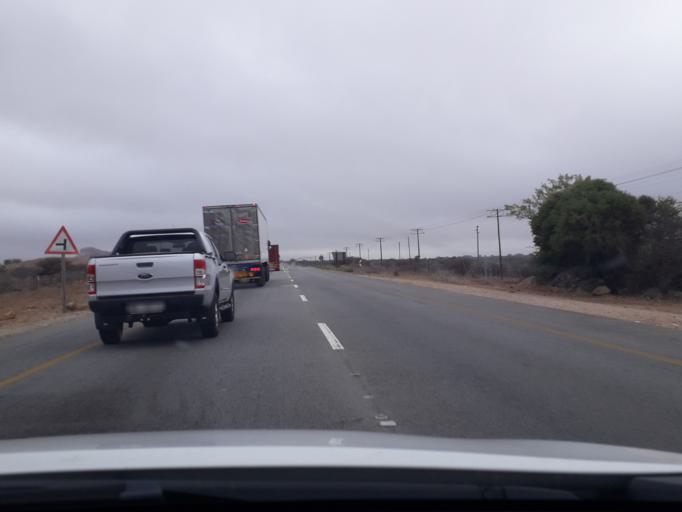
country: ZA
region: Limpopo
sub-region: Capricorn District Municipality
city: Mankoeng
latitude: -23.5230
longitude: 29.7078
